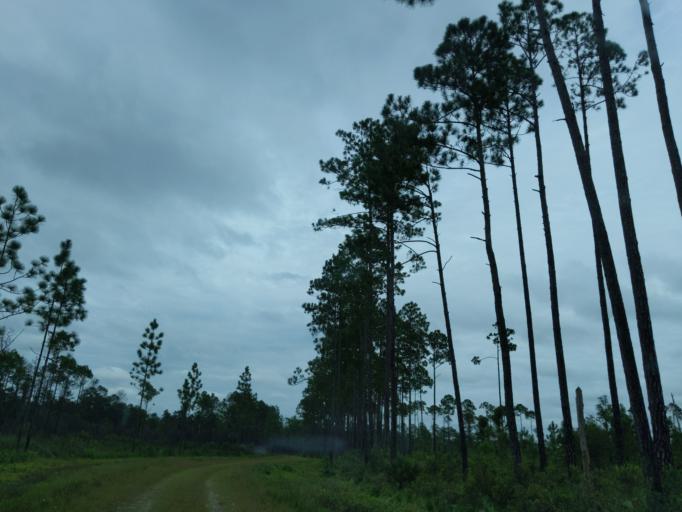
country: US
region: Florida
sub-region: Gadsden County
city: Midway
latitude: 30.3524
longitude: -84.4894
